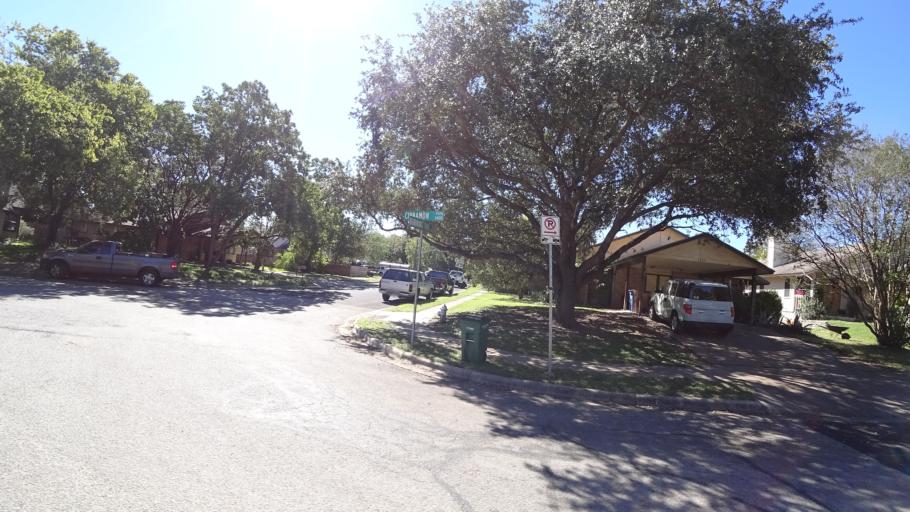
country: US
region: Texas
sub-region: Travis County
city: Austin
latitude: 30.2397
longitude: -97.7731
